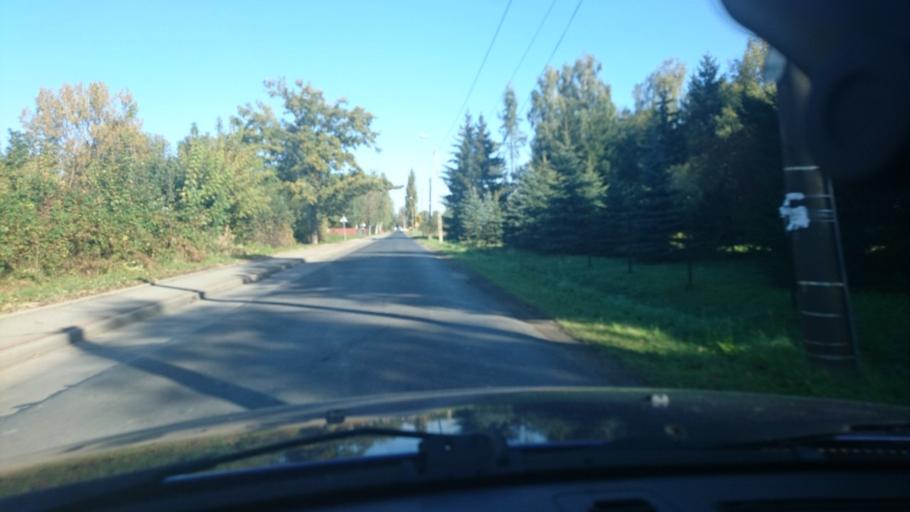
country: PL
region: Silesian Voivodeship
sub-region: Powiat bielski
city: Bronow
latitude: 49.8549
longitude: 18.9438
